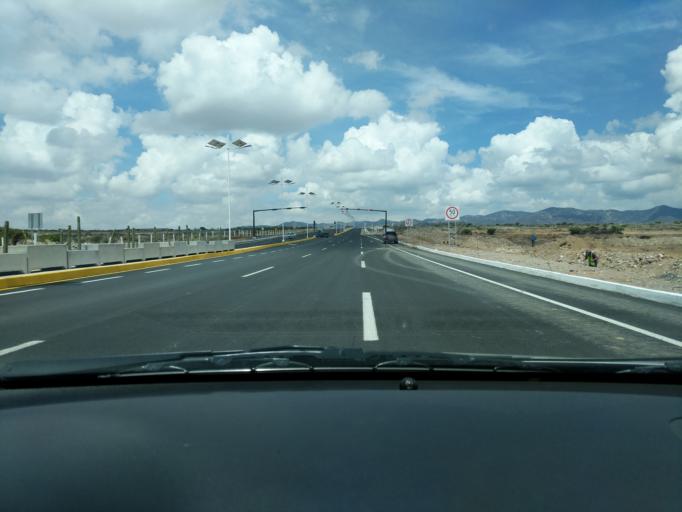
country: MX
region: San Luis Potosi
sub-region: Mexquitic de Carmona
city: Guadalupe Victoria
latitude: 22.1661
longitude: -101.0515
